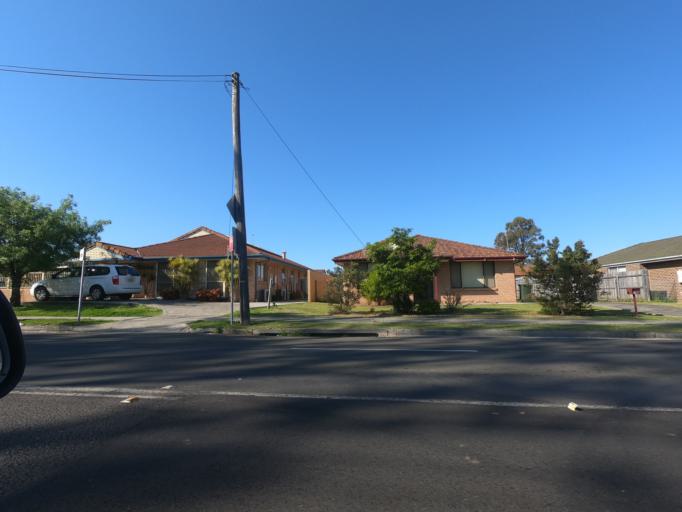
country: AU
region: New South Wales
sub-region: Wollongong
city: Dapto
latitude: -34.4911
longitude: 150.7786
